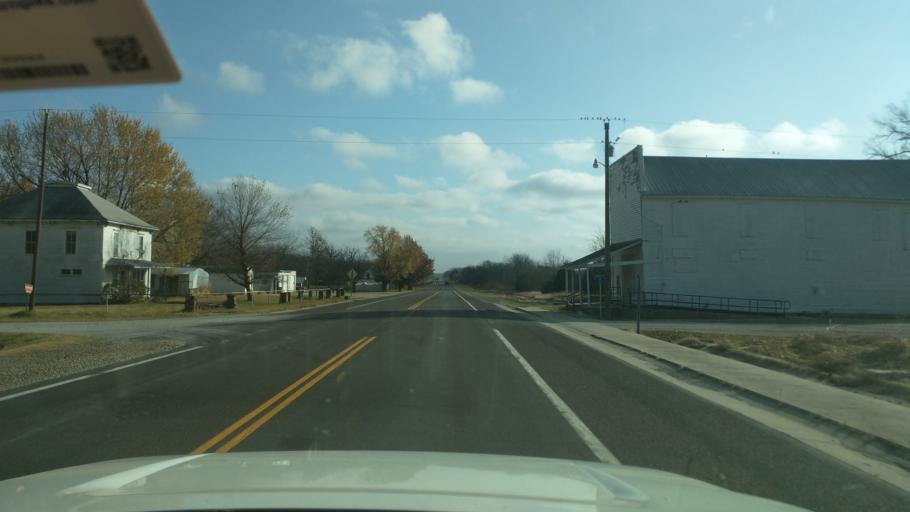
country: US
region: Kansas
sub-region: Montgomery County
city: Caney
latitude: 37.0679
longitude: -96.0144
